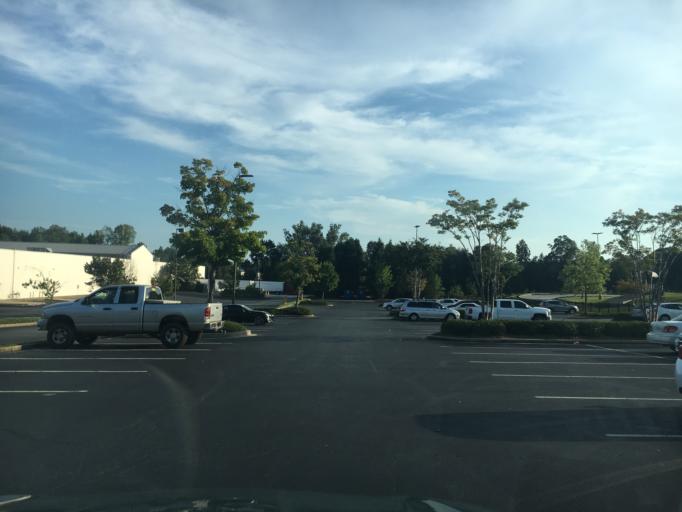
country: US
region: South Carolina
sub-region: Greenville County
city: Mauldin
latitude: 34.8215
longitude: -82.2950
